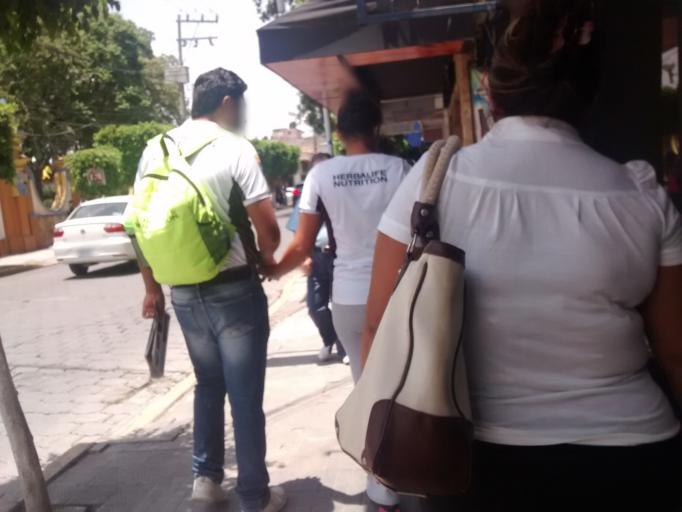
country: MX
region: Puebla
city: Tehuacan
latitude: 18.4656
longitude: -97.3941
